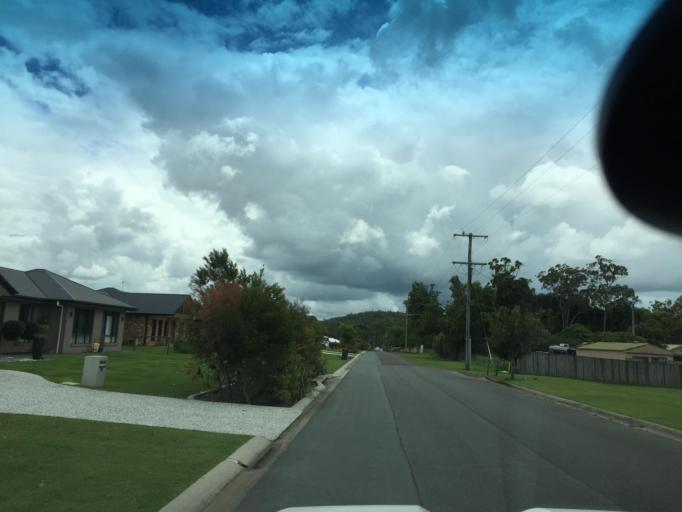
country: AU
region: Queensland
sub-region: Moreton Bay
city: Caboolture
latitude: -27.0438
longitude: 152.9296
